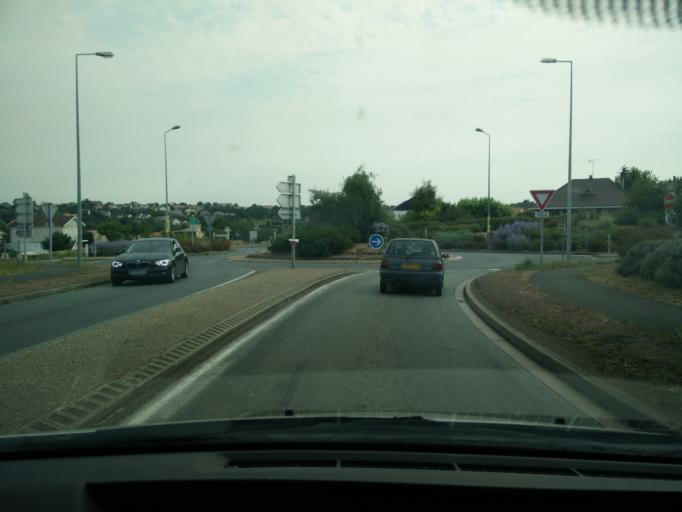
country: FR
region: Poitou-Charentes
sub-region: Departement des Deux-Sevres
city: Saint-Jean-de-Thouars
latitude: 46.9691
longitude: -0.2095
